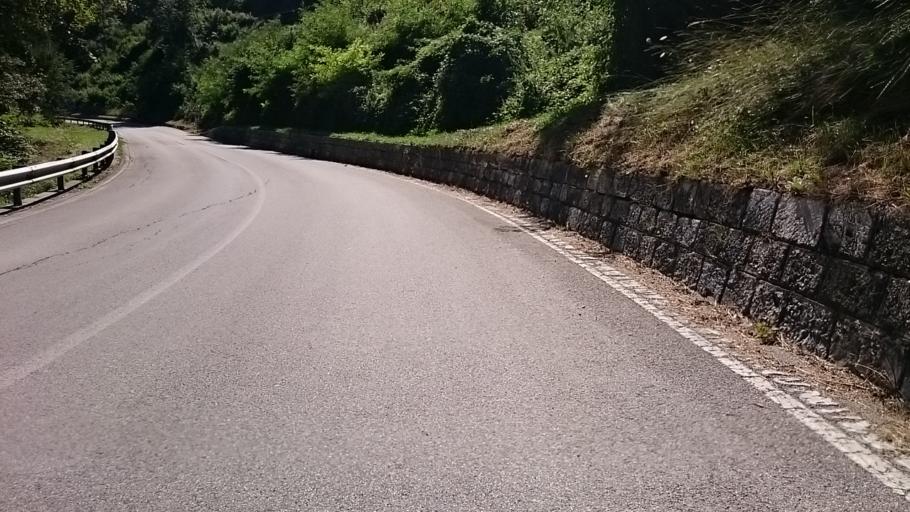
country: IT
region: Veneto
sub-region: Provincia di Belluno
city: Ospitale di Cadore
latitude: 46.3247
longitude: 12.3175
